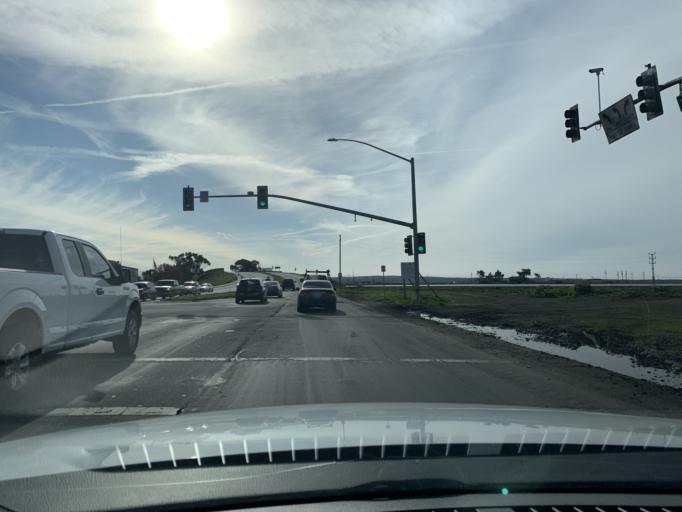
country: US
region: California
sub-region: Monterey County
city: Boronda
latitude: 36.6886
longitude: -121.6720
